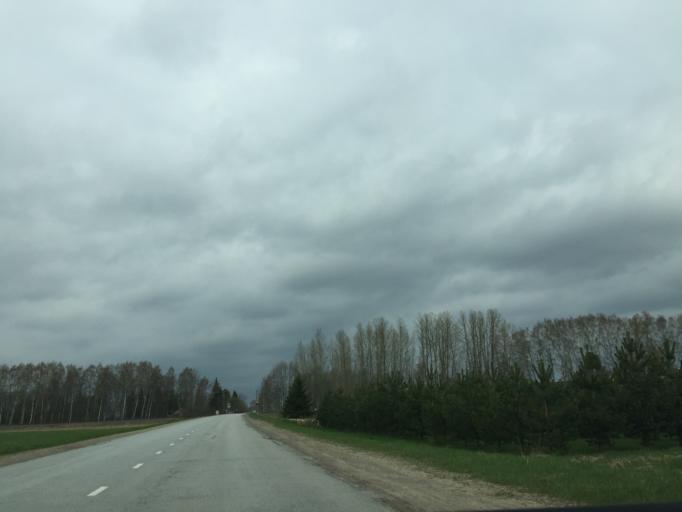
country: EE
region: Tartu
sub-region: Noo vald
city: Noo
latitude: 58.2781
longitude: 26.5292
